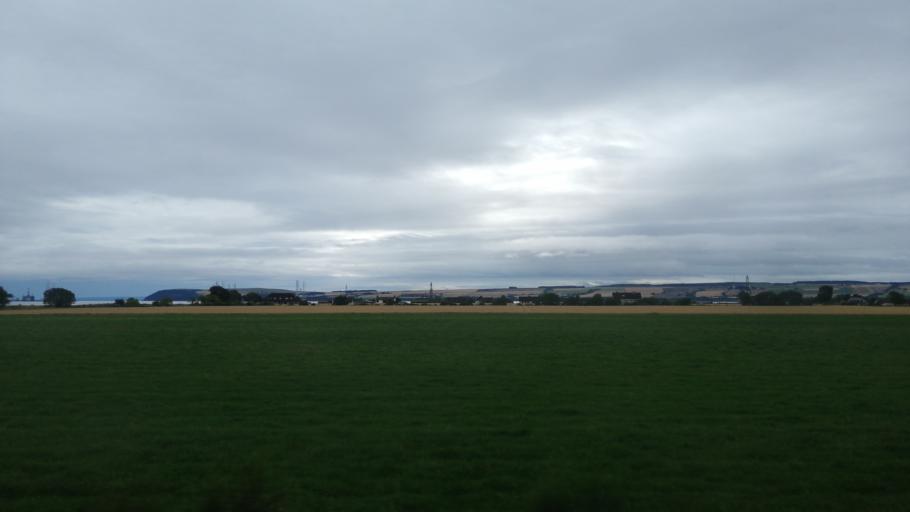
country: GB
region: Scotland
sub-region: Highland
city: Invergordon
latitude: 57.7059
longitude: -4.1413
